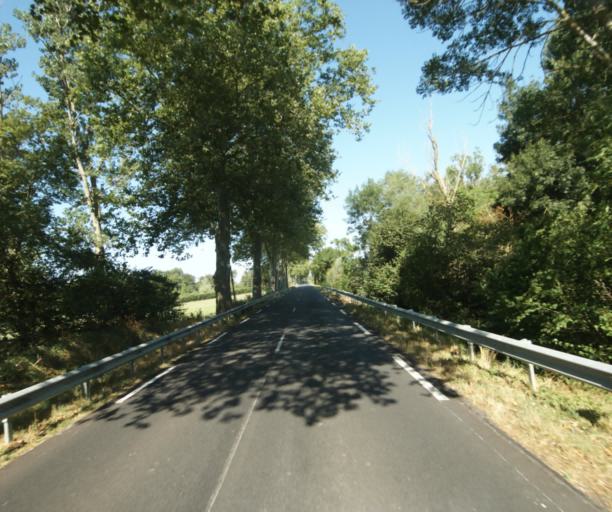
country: FR
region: Midi-Pyrenees
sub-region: Departement de la Haute-Garonne
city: Revel
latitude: 43.4681
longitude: 1.9712
